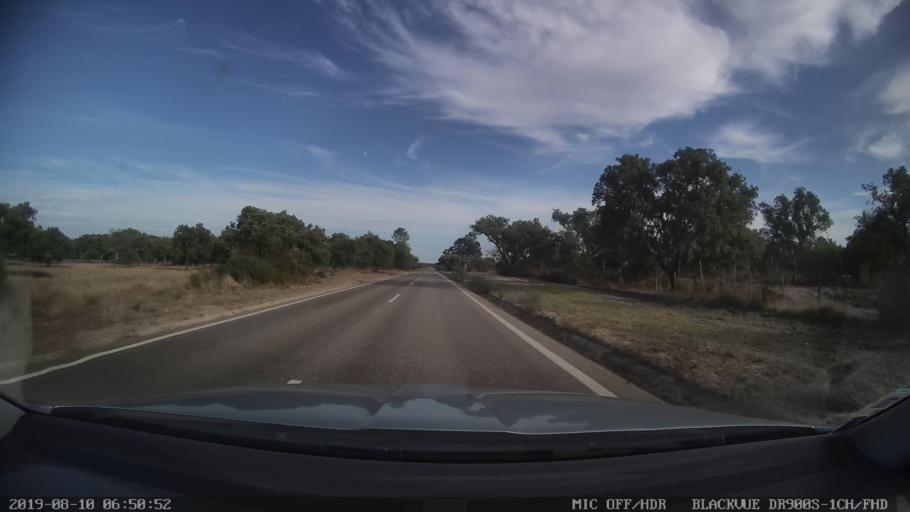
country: PT
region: Santarem
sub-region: Benavente
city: Poceirao
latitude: 38.9003
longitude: -8.7553
